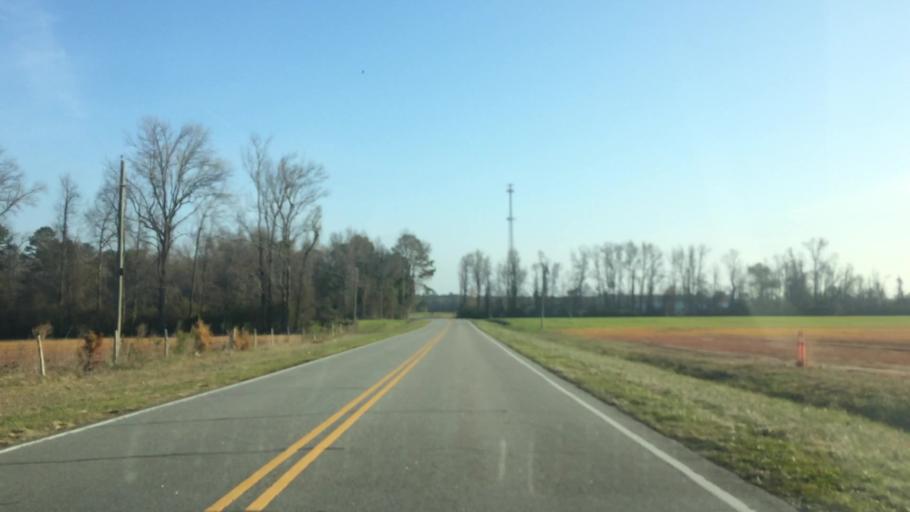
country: US
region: North Carolina
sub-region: Edgecombe County
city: Pinetops
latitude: 35.6988
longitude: -77.6359
